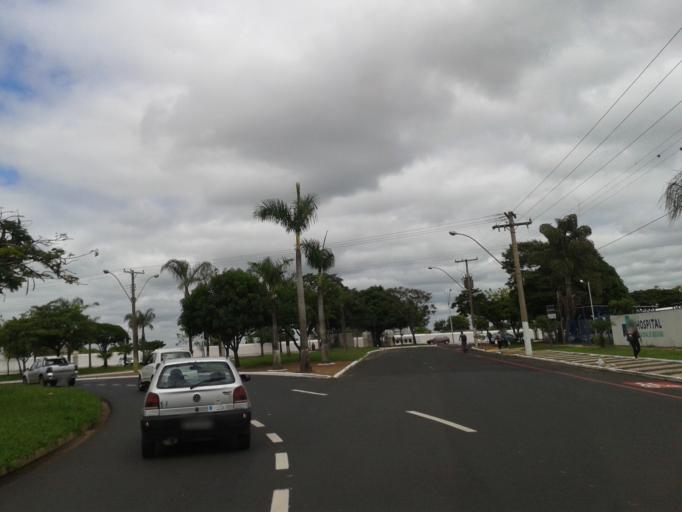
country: BR
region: Minas Gerais
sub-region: Uberaba
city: Uberaba
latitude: -19.7423
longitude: -47.9593
